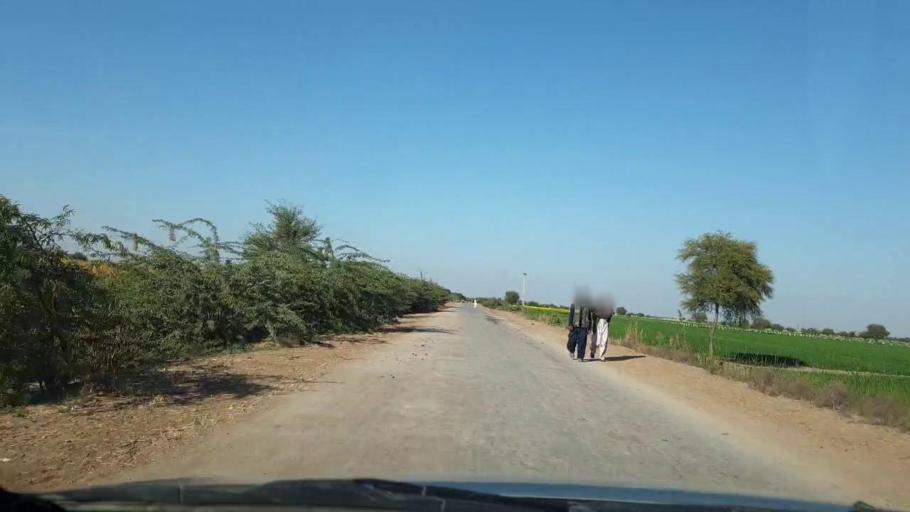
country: PK
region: Sindh
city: Berani
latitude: 25.8217
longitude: 68.9479
